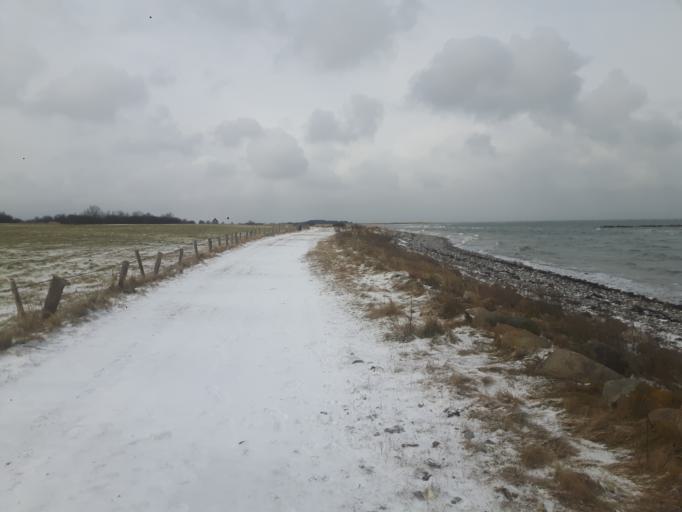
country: DE
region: Schleswig-Holstein
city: Fehmarn
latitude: 54.5066
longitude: 11.2071
